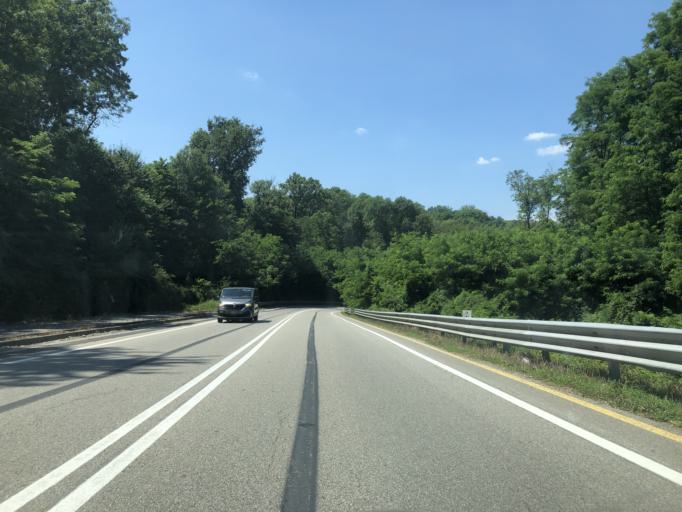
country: IT
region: Piedmont
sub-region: Provincia di Novara
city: Oleggio Castello
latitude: 45.7497
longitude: 8.5383
